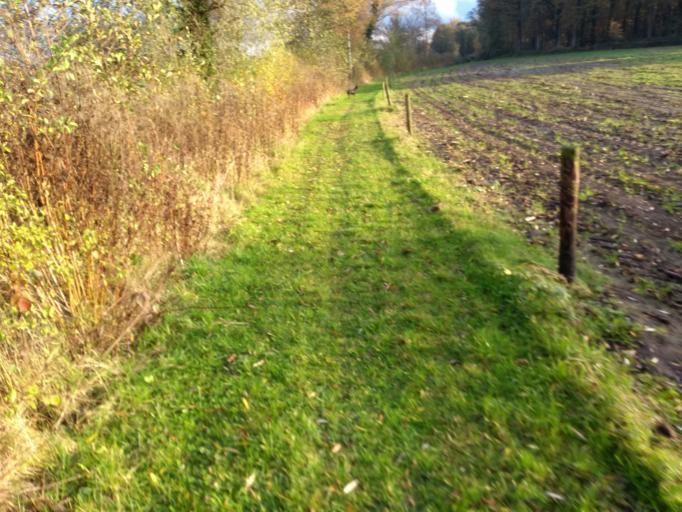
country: NL
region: Overijssel
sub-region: Gemeente Borne
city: Borne
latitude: 52.3404
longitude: 6.7328
